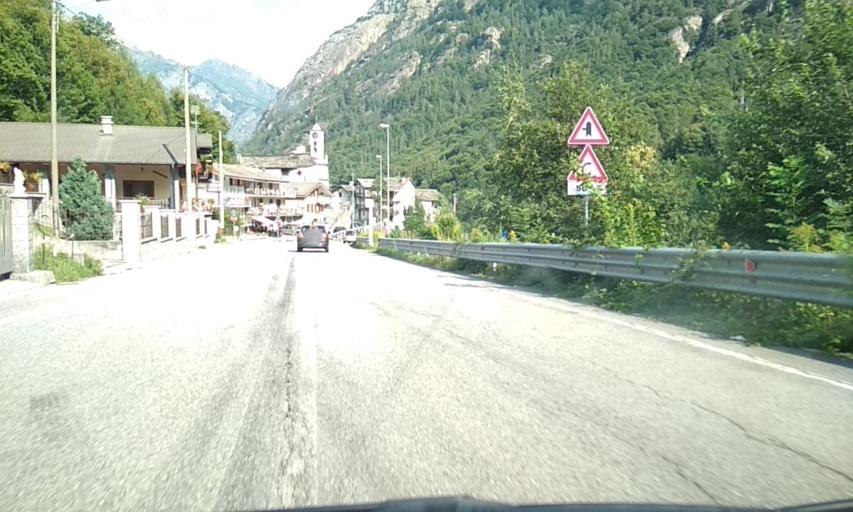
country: IT
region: Piedmont
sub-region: Provincia di Torino
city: Locana
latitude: 45.4304
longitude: 7.3943
